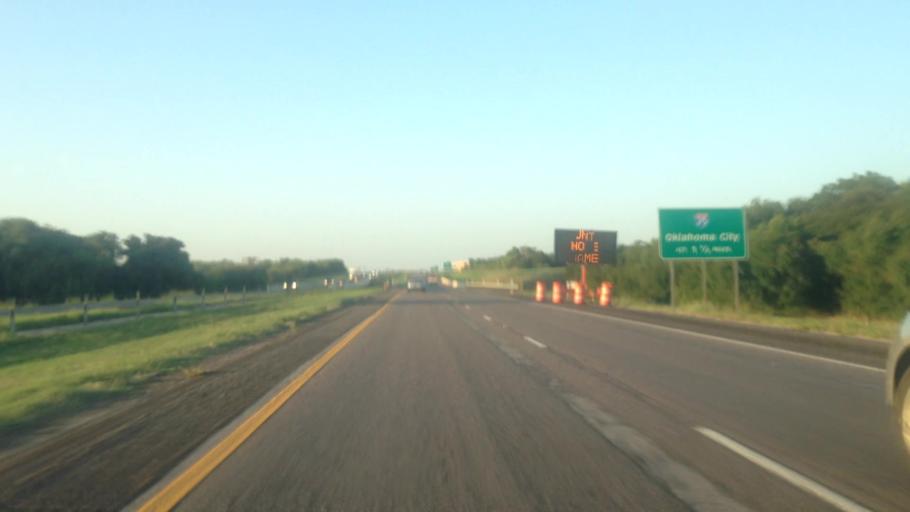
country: US
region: Texas
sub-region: Denton County
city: Denton
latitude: 33.1837
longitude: -97.1738
